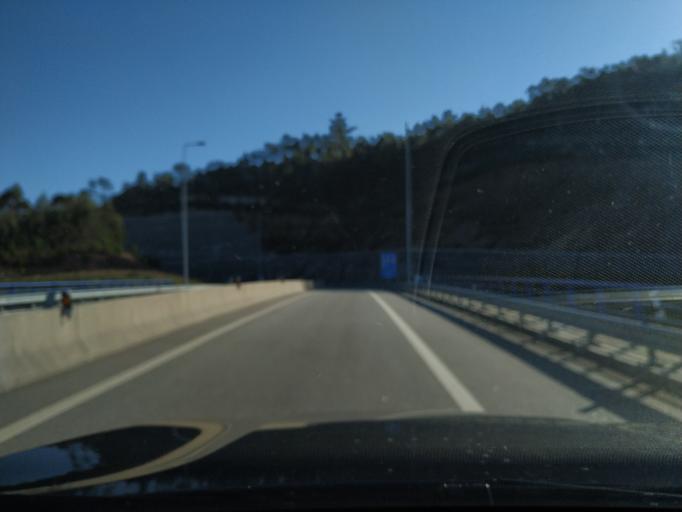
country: PT
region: Aveiro
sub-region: Oliveira de Azemeis
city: Vila Cha
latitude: 40.8747
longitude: -8.4318
